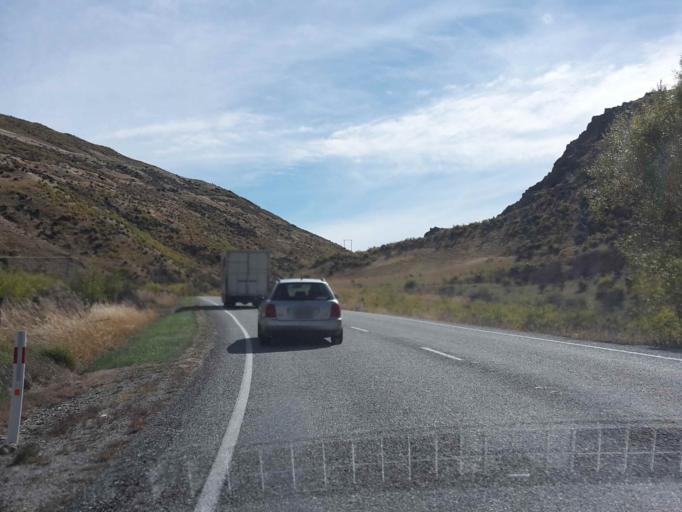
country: NZ
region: Otago
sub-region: Queenstown-Lakes District
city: Wanaka
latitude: -44.7322
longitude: 169.5090
